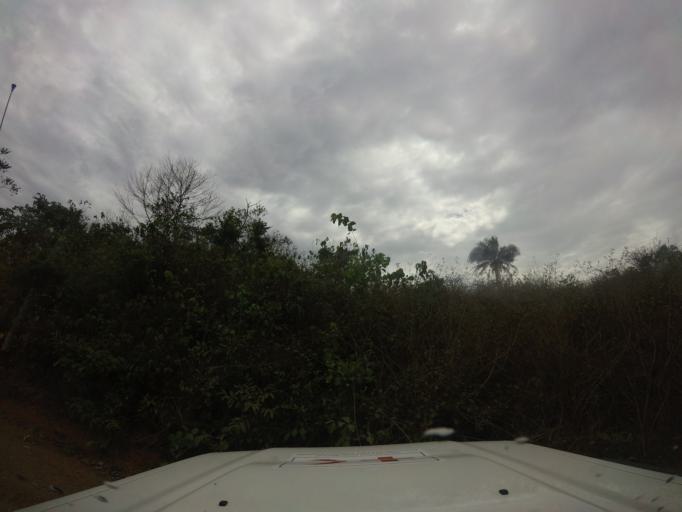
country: SL
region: Southern Province
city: Zimmi
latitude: 7.2321
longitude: -11.1973
